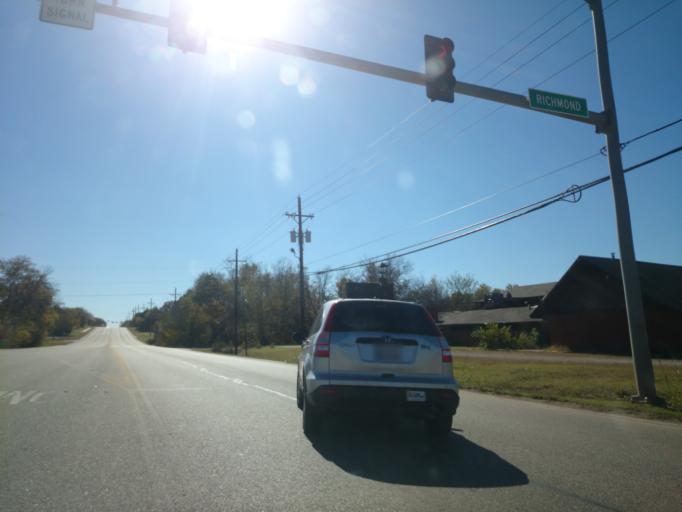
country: US
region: Oklahoma
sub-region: Payne County
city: Stillwater
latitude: 36.1738
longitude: -97.0698
